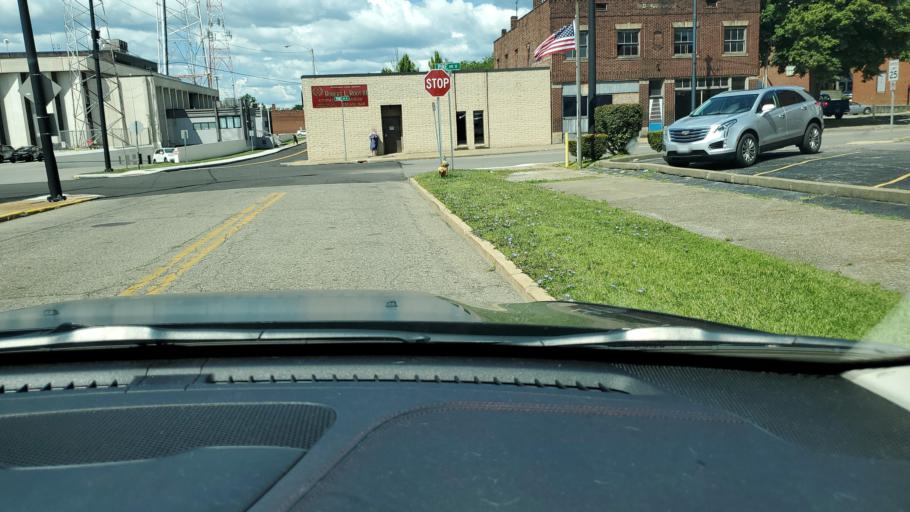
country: US
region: Ohio
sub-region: Trumbull County
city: Warren
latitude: 41.2350
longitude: -80.8158
